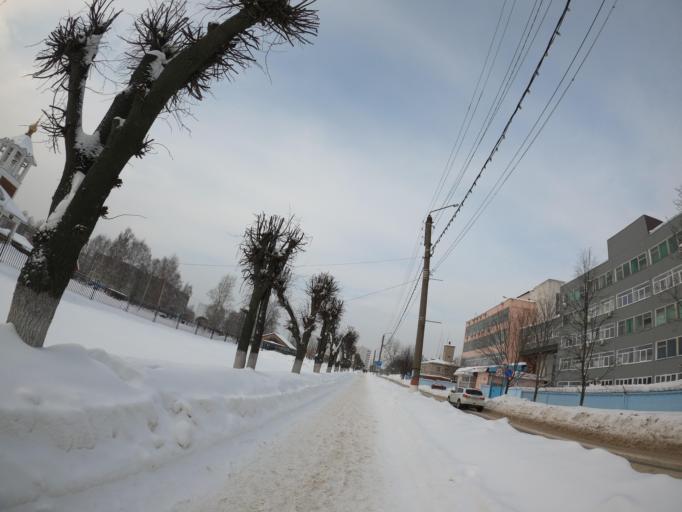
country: RU
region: Moskovskaya
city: Elektrogorsk
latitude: 55.8856
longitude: 38.7817
